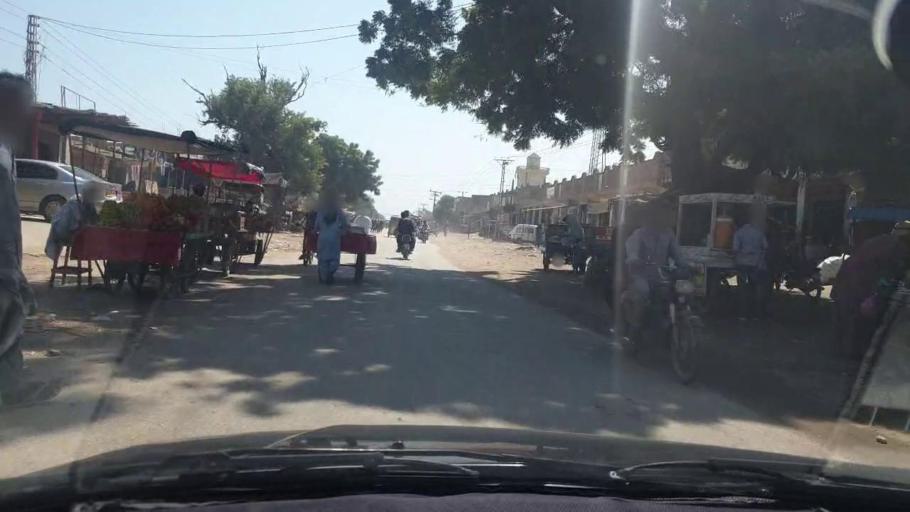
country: PK
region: Sindh
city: Tando Allahyar
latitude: 25.4529
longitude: 68.7237
